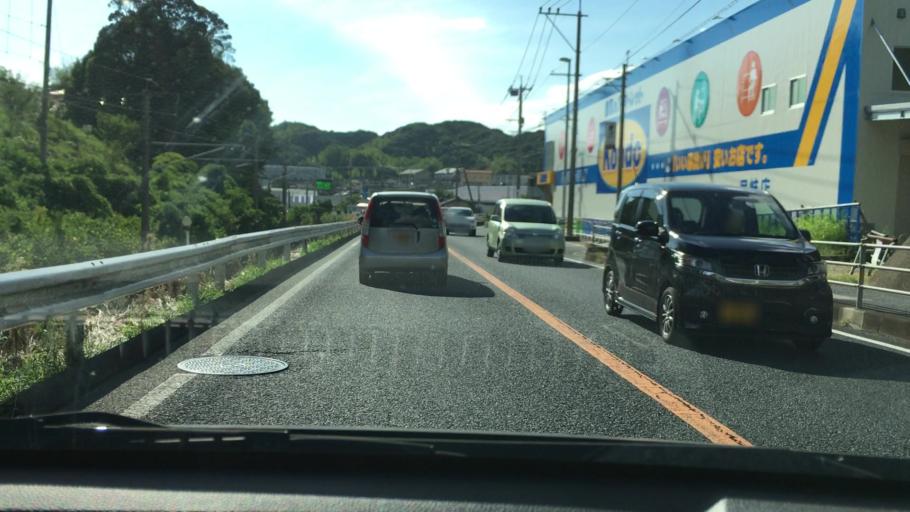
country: JP
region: Nagasaki
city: Sasebo
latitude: 33.1447
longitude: 129.8087
